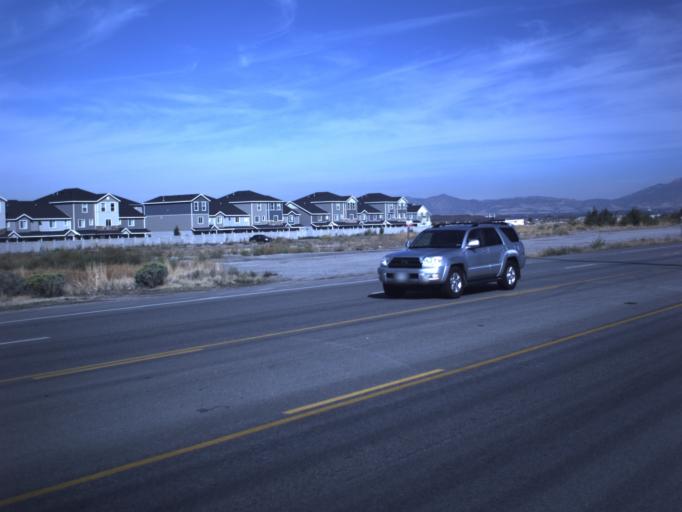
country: US
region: Utah
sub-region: Utah County
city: Orem
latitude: 40.3006
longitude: -111.7338
